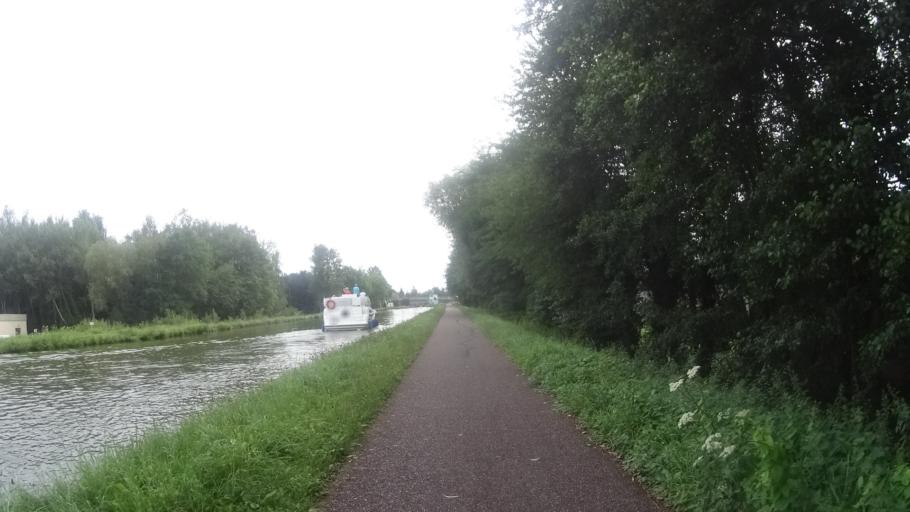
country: FR
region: Alsace
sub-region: Departement du Bas-Rhin
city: Steinbourg
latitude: 48.7617
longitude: 7.4131
